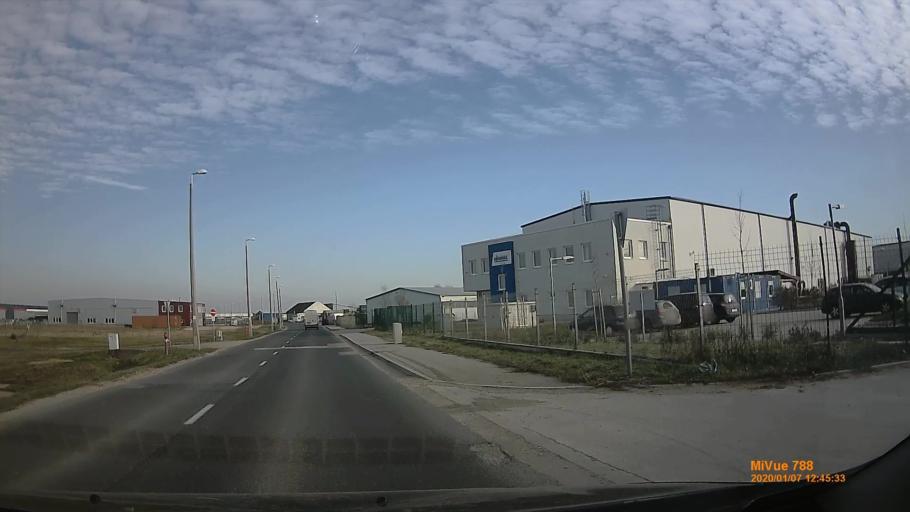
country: HU
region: Gyor-Moson-Sopron
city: Toltestava
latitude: 47.6772
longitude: 17.7113
